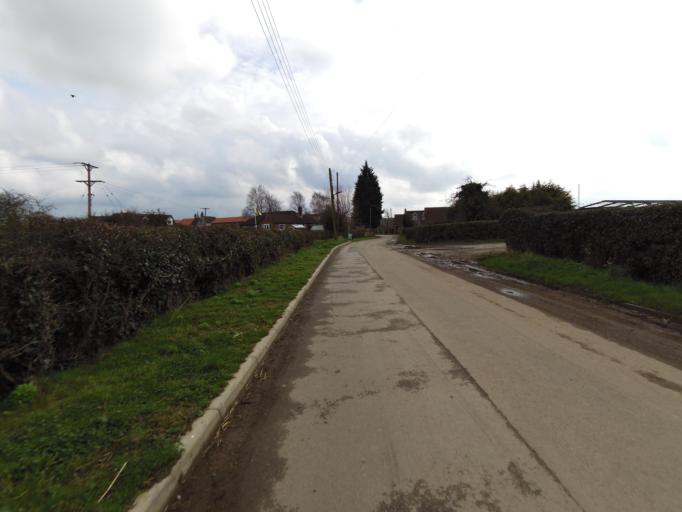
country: GB
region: England
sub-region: Doncaster
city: Moss
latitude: 53.6057
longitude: -1.0687
